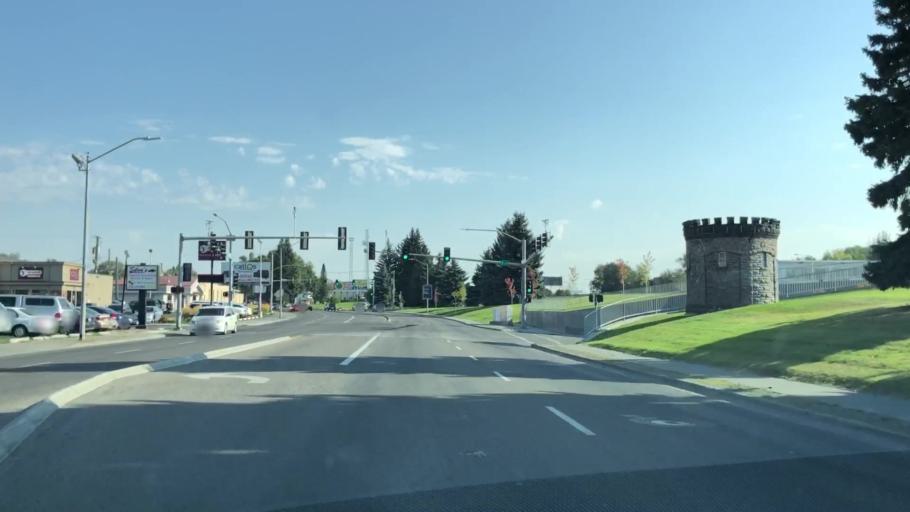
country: US
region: Idaho
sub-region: Bonneville County
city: Idaho Falls
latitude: 43.4937
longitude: -112.0369
